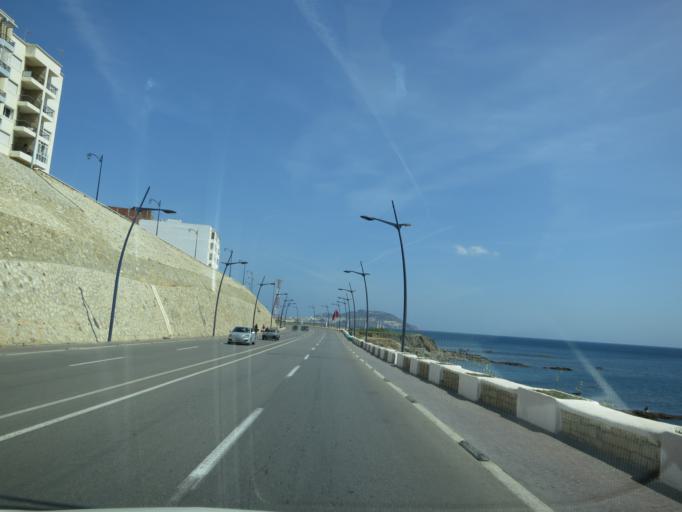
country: ES
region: Ceuta
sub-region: Ceuta
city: Ceuta
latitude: 35.8526
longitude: -5.3497
